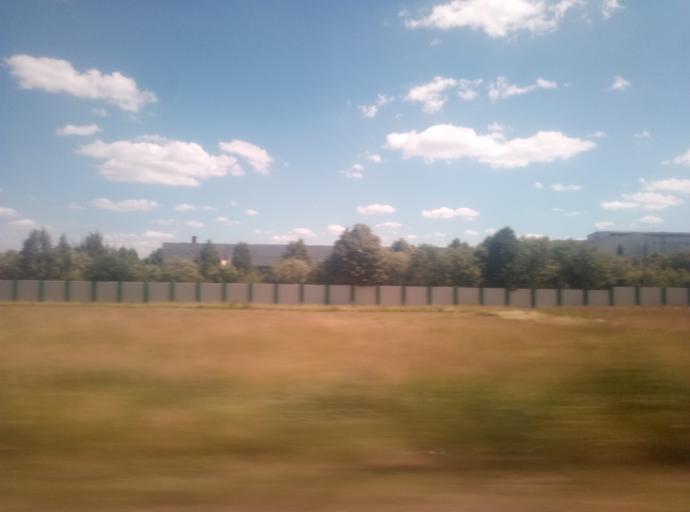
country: RU
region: Tula
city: Kireyevsk
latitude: 53.9598
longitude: 37.9380
